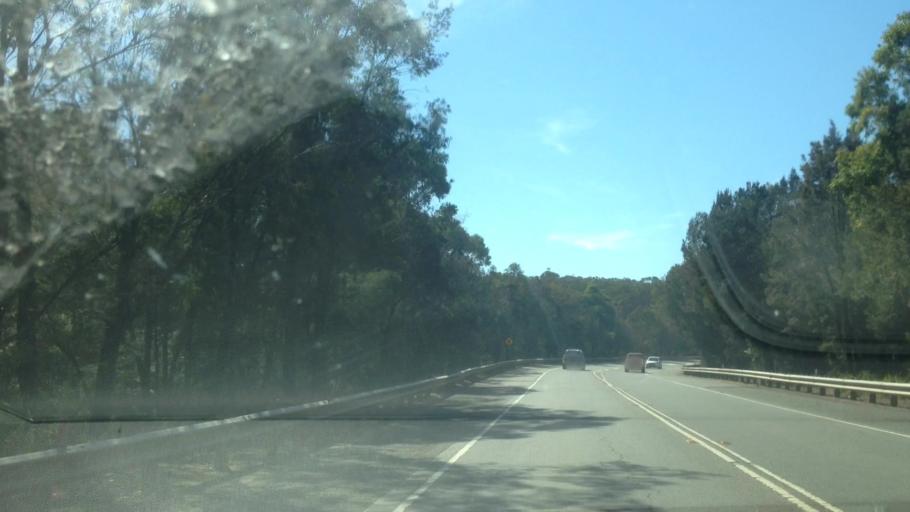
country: AU
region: New South Wales
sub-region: Lake Macquarie Shire
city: Toronto
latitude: -32.9862
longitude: 151.5144
